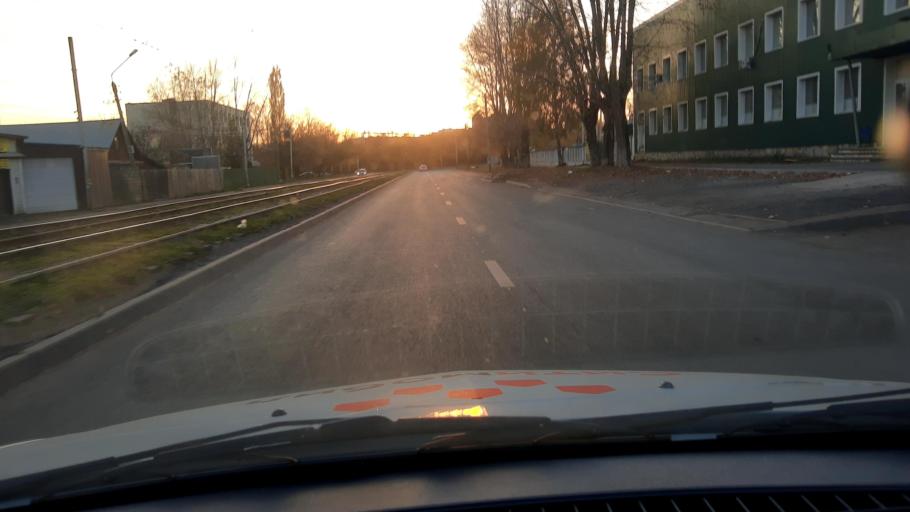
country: RU
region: Bashkortostan
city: Ufa
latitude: 54.8249
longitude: 56.0888
